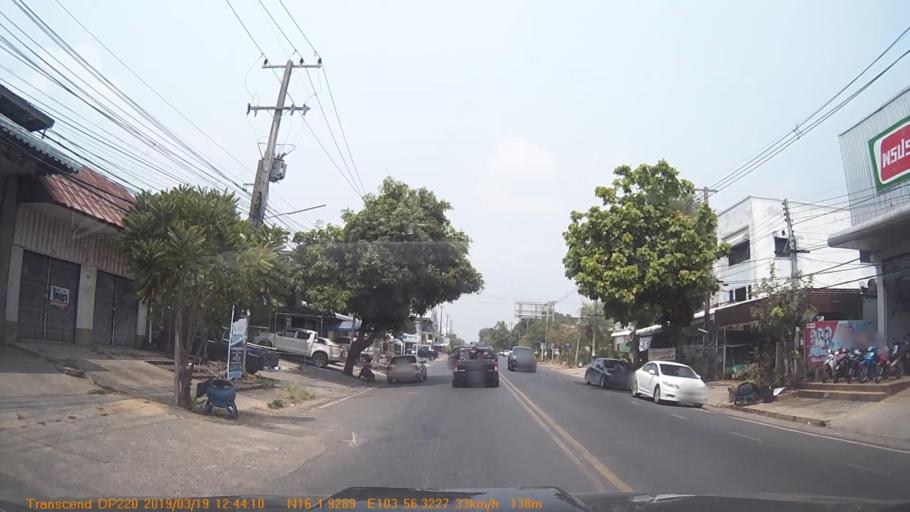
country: TH
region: Roi Et
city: Selaphum
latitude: 16.0323
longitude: 103.9387
